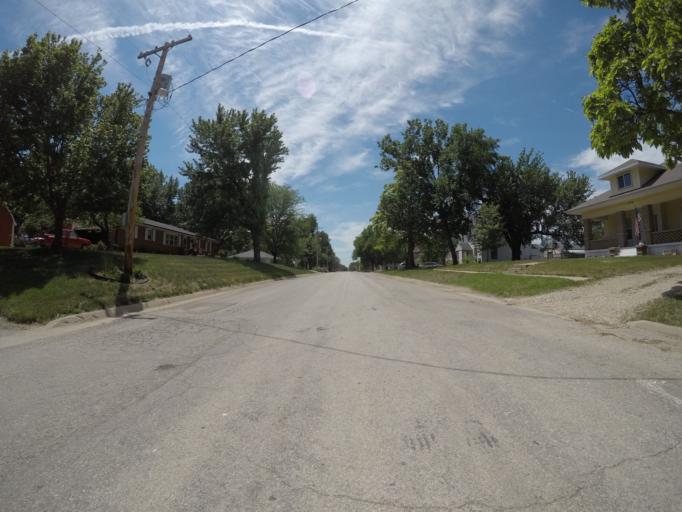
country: US
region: Kansas
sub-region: Wabaunsee County
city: Alma
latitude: 39.0206
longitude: -96.2888
